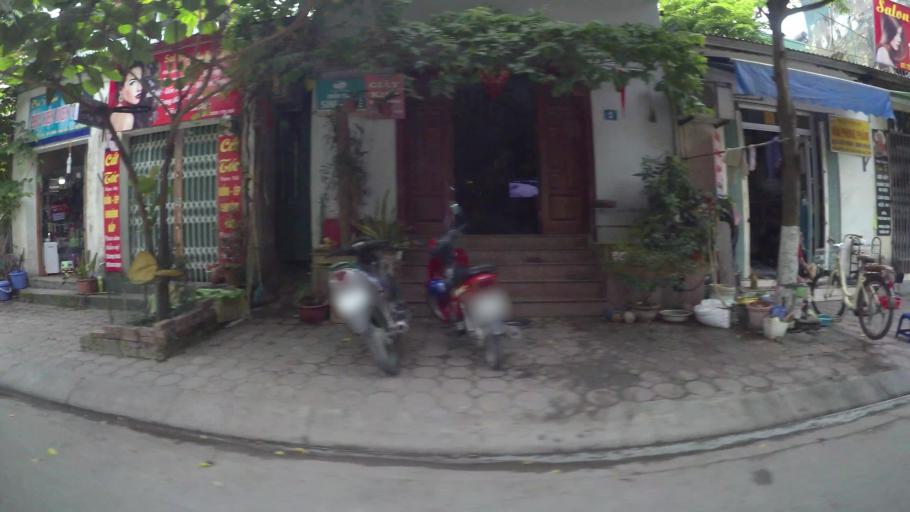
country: VN
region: Ha Noi
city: Trau Quy
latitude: 21.0440
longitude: 105.9263
